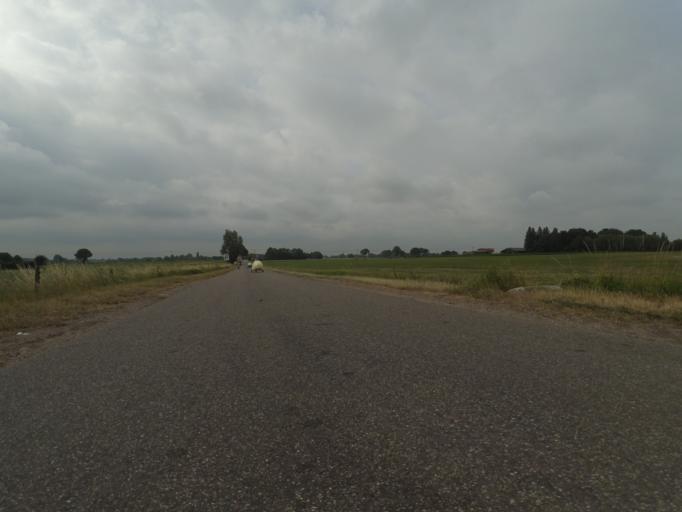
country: BE
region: Flanders
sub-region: Provincie Antwerpen
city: Essen
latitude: 51.4577
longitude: 4.4082
